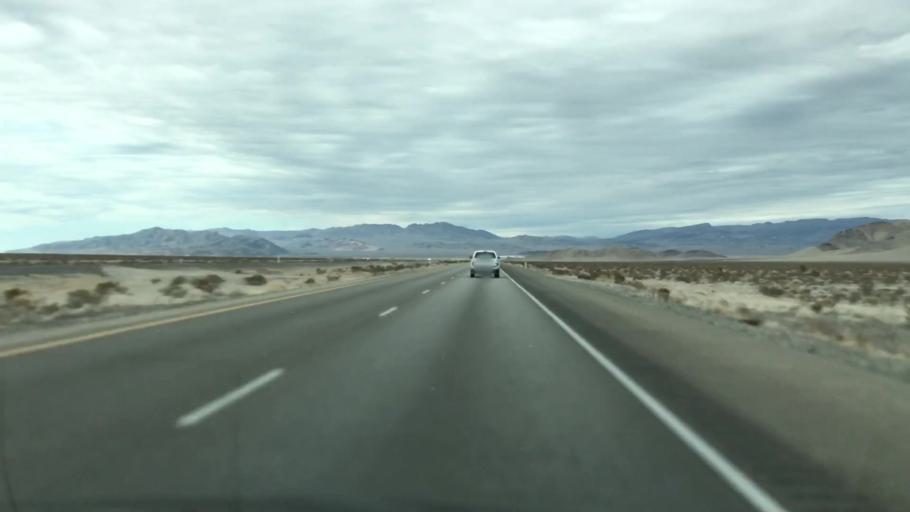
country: US
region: Nevada
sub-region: Nye County
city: Pahrump
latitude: 36.5643
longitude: -115.6183
